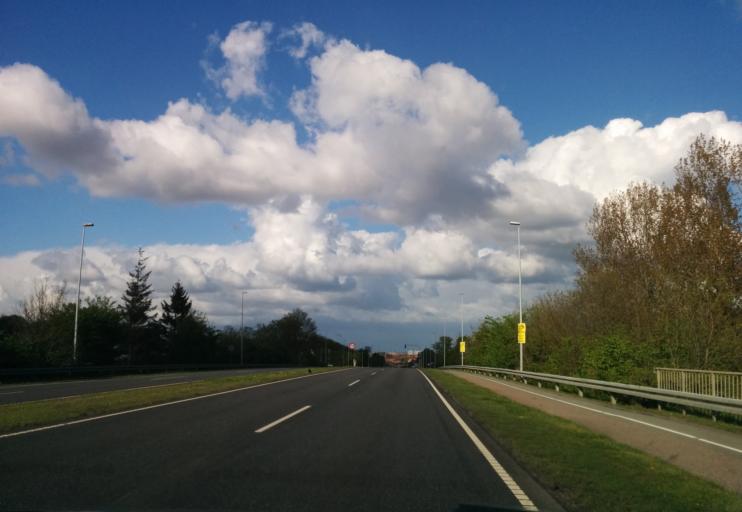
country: DK
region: Central Jutland
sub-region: Arhus Kommune
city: Stavtrup
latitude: 56.1168
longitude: 10.1375
